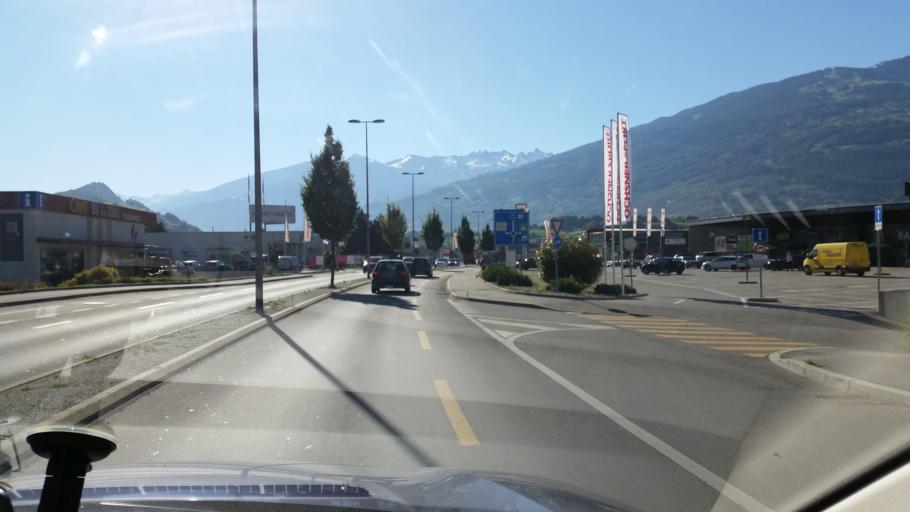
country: CH
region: Valais
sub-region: Conthey District
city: Vetroz
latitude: 46.2253
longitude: 7.2944
